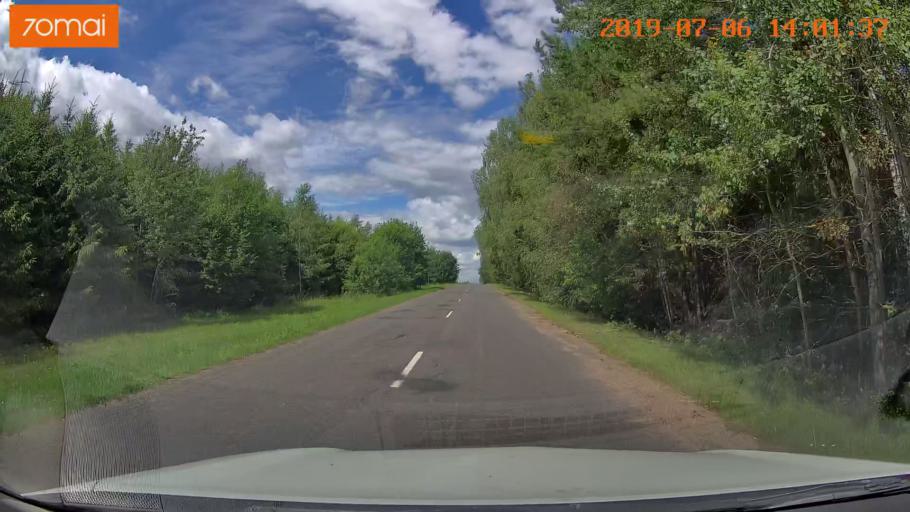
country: BY
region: Minsk
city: Ivyanyets
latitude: 53.8104
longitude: 26.8119
